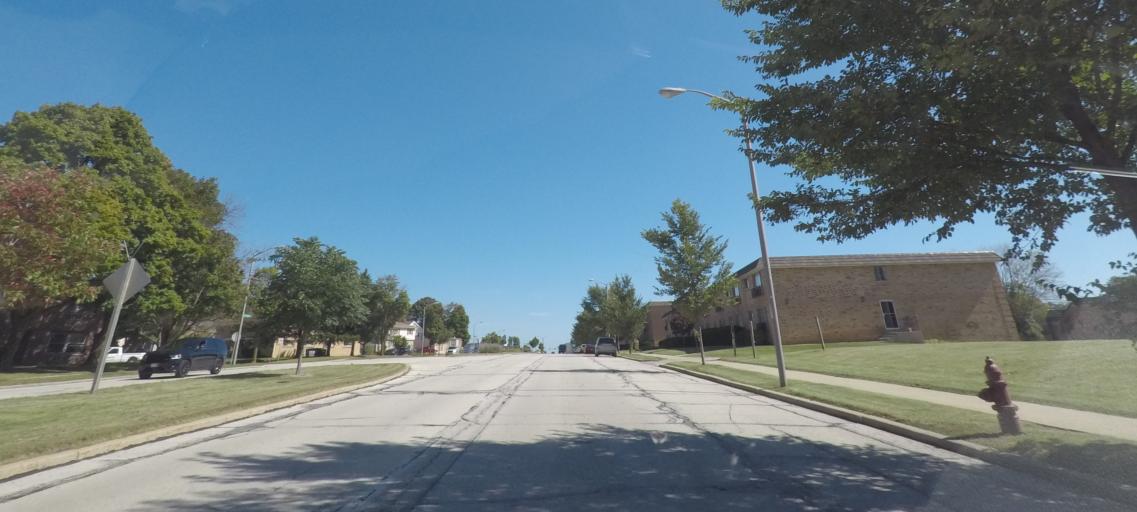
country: US
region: Wisconsin
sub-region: Milwaukee County
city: West Allis
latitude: 43.0004
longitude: -88.0350
